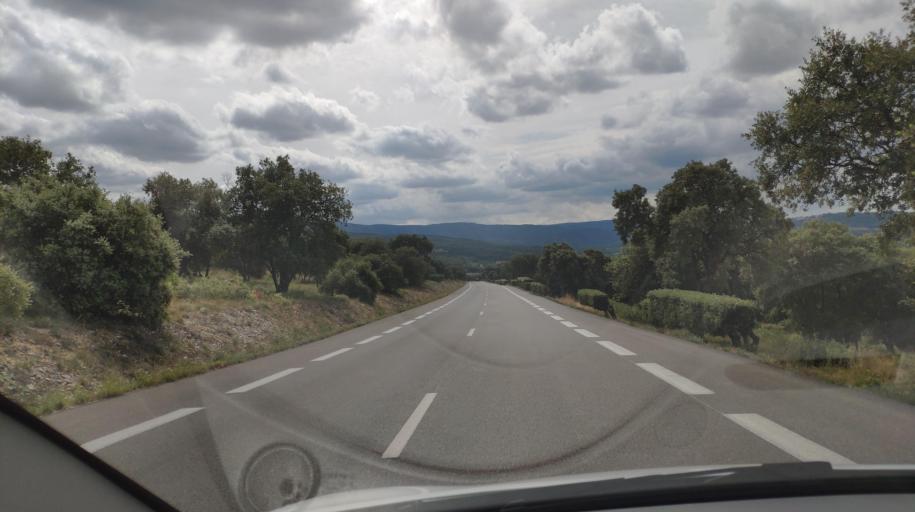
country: FR
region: Provence-Alpes-Cote d'Azur
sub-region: Departement du Vaucluse
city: Villes-sur-Auzon
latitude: 44.0623
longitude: 5.2442
